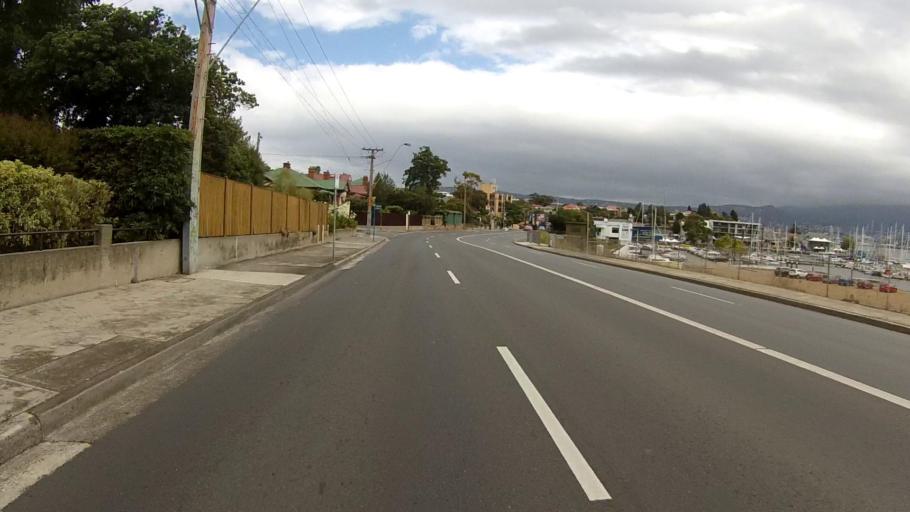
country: AU
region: Tasmania
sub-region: Clarence
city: Bellerive
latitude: -42.8725
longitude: 147.3696
